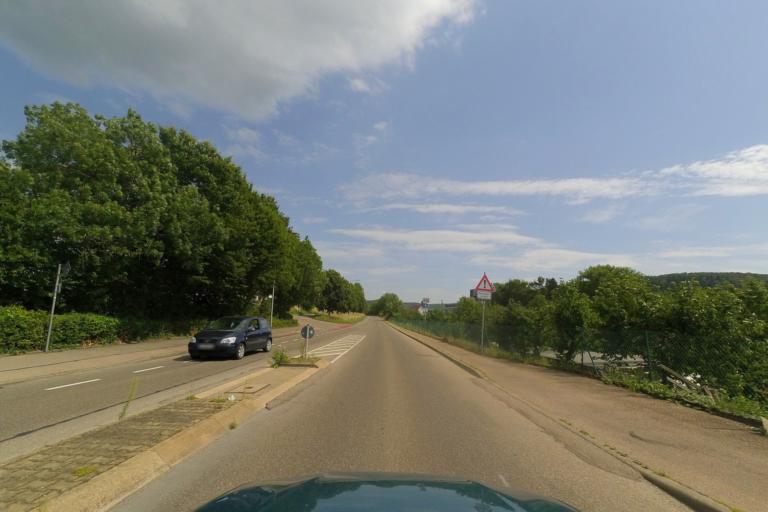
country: DE
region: Baden-Wuerttemberg
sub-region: Regierungsbezirk Stuttgart
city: Aalen
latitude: 48.8320
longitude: 10.1070
